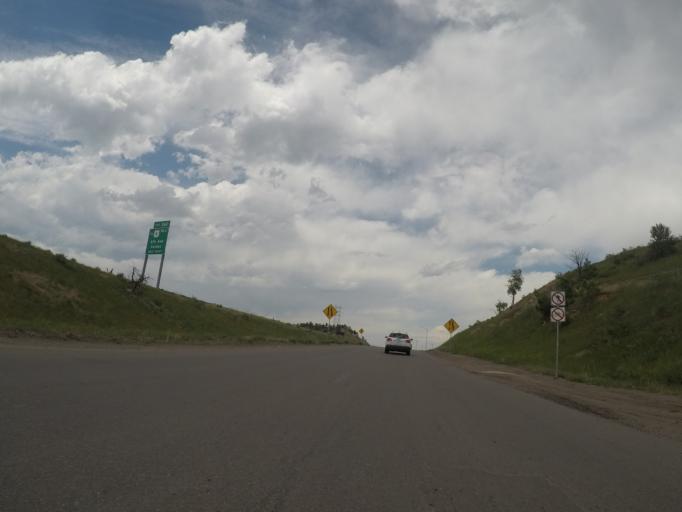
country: US
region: Colorado
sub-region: Jefferson County
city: West Pleasant View
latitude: 39.6989
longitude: -105.2039
